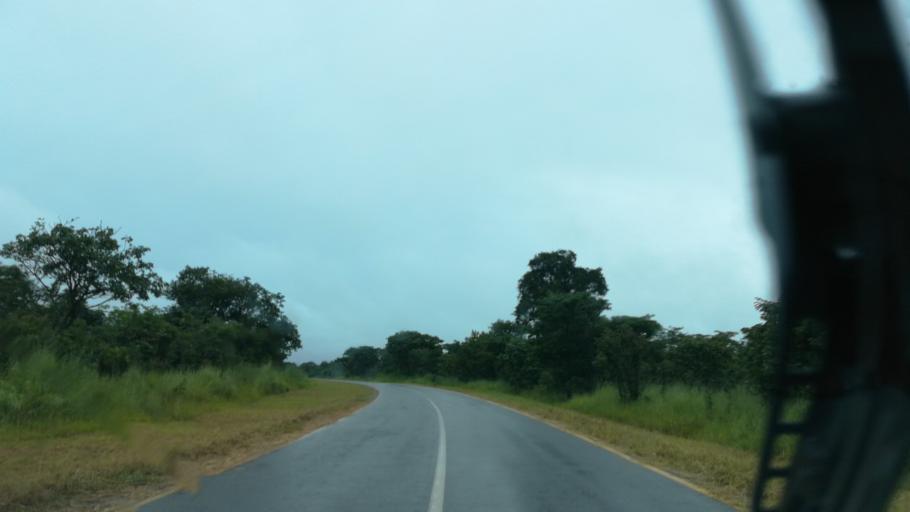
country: ZM
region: Luapula
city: Mwense
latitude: -10.8257
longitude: 28.2354
